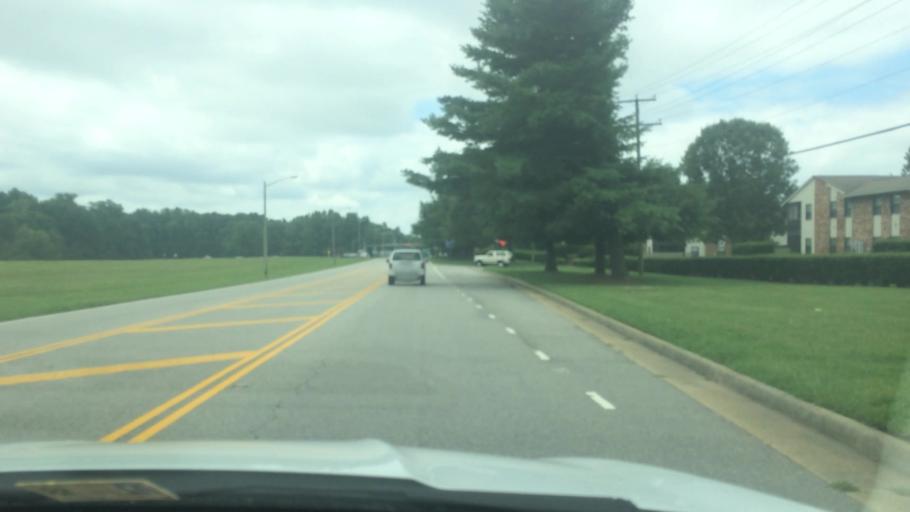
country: US
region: Virginia
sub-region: York County
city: Yorktown
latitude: 37.2105
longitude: -76.5727
